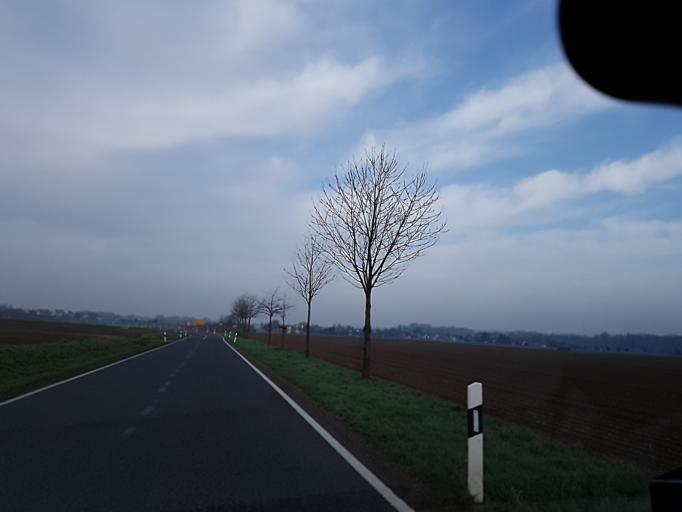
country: DE
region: Saxony
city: Naundorf
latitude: 51.2373
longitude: 13.0907
